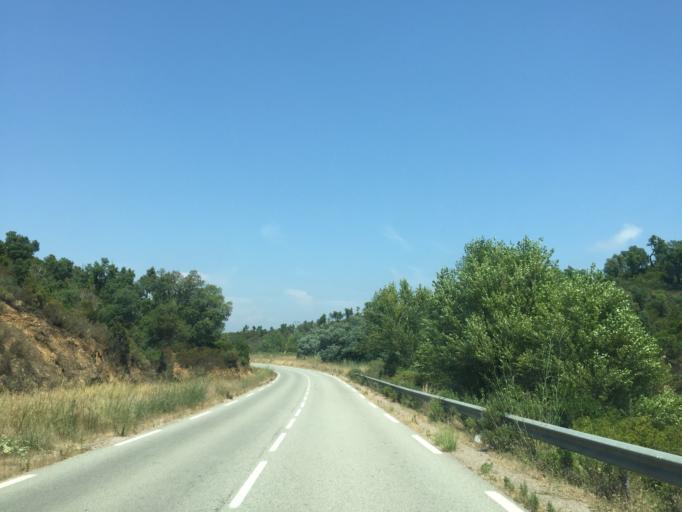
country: FR
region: Provence-Alpes-Cote d'Azur
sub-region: Departement du Var
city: Roquebrune-sur-Argens
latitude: 43.3815
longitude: 6.6754
